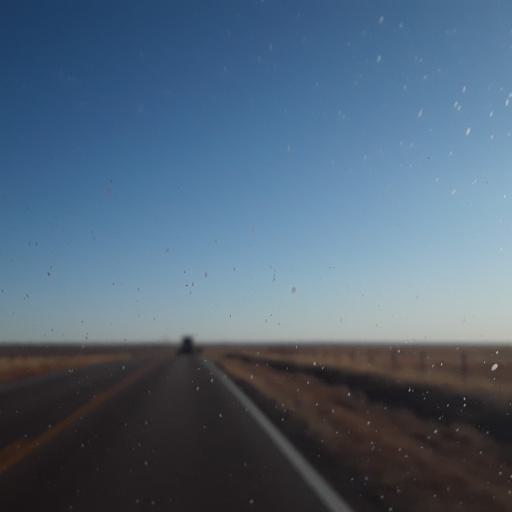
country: US
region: Kansas
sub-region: Wallace County
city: Sharon Springs
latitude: 39.0237
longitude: -101.7387
